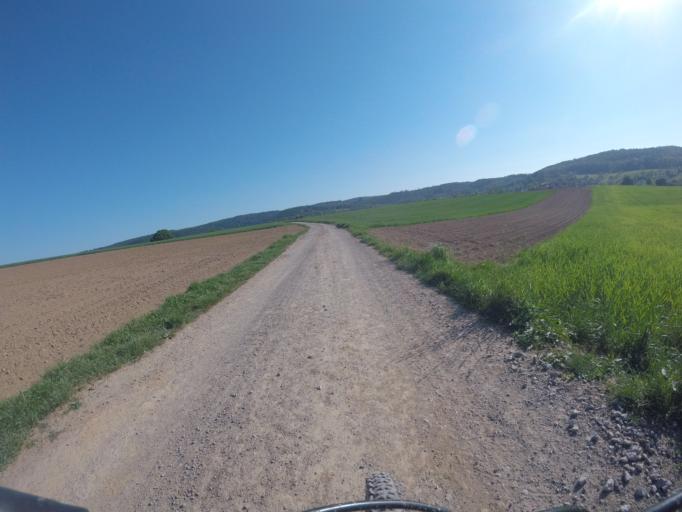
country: DE
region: Baden-Wuerttemberg
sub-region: Regierungsbezirk Stuttgart
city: Aspach
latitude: 48.9838
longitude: 9.4018
